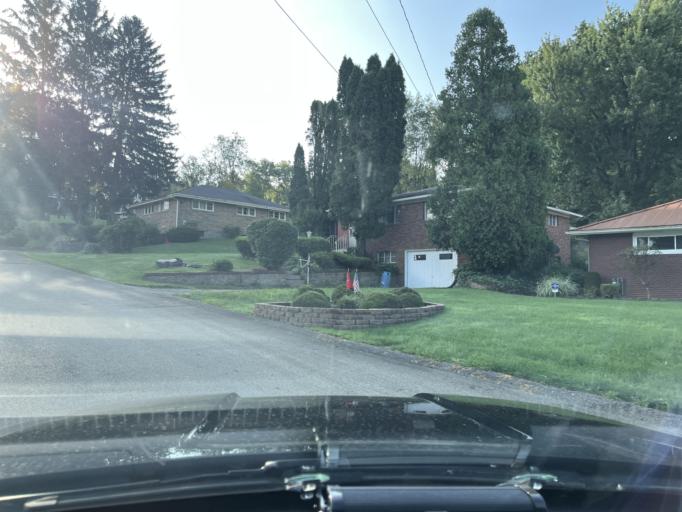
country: US
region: Pennsylvania
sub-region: Fayette County
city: Leith-Hatfield
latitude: 39.8840
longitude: -79.7279
